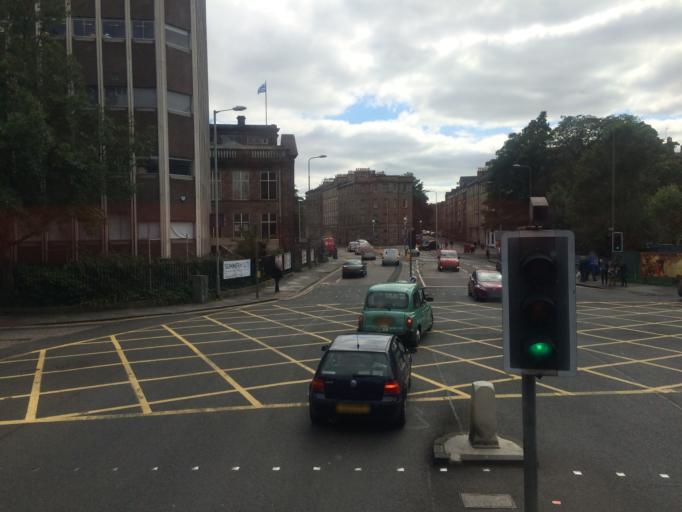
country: GB
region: Scotland
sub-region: Edinburgh
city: Edinburgh
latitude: 55.9407
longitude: -3.1828
